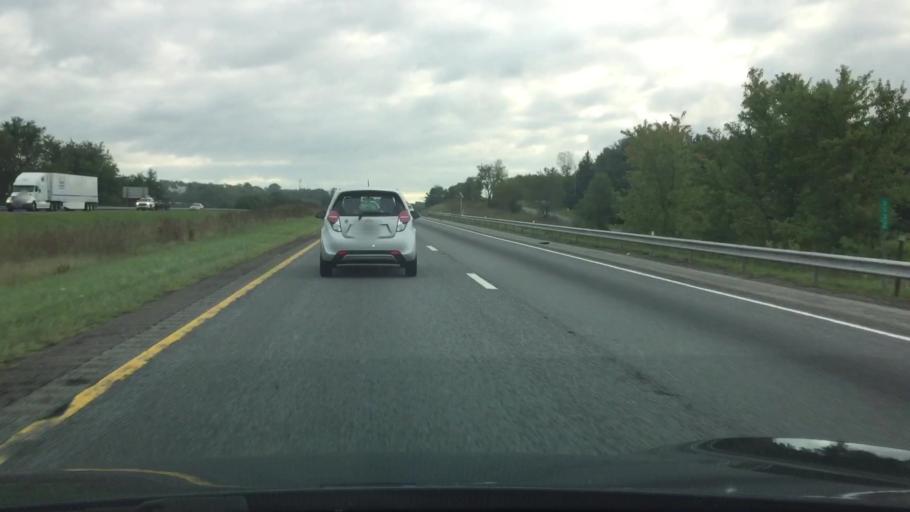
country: US
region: Virginia
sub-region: Montgomery County
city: Christiansburg
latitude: 37.1120
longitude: -80.4427
